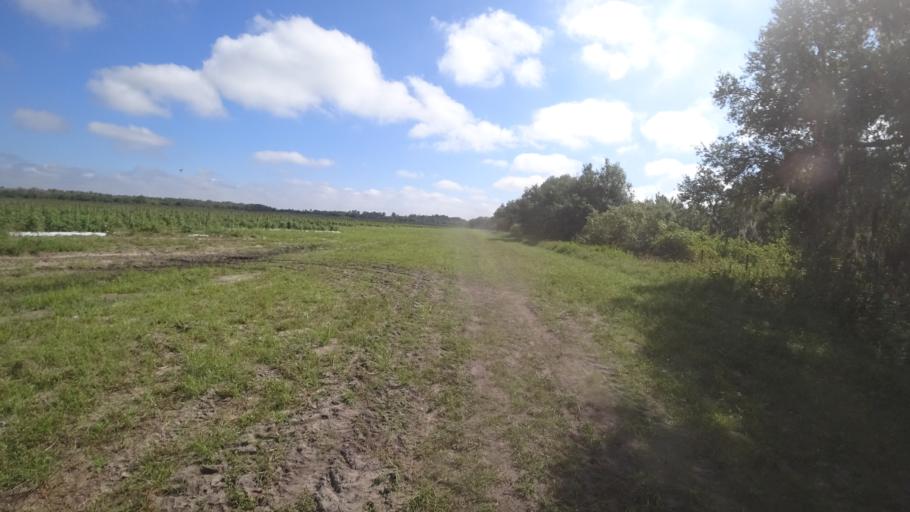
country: US
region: Florida
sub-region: DeSoto County
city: Arcadia
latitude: 27.2817
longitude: -82.0832
